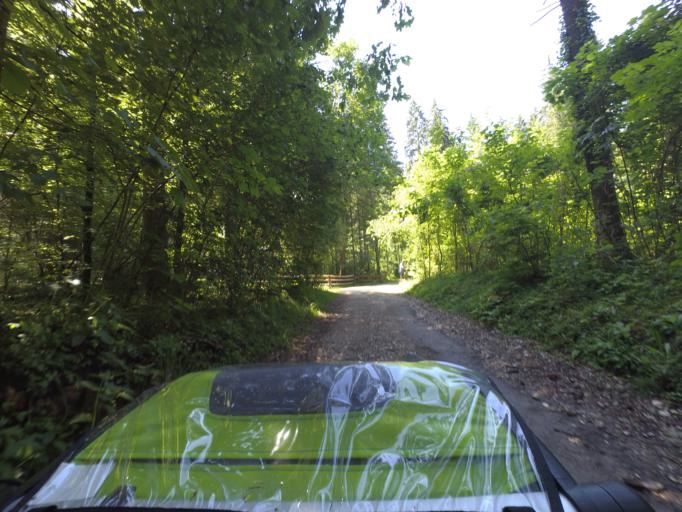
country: DE
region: Bavaria
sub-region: Upper Bavaria
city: Bayerisch Gmain
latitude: 47.7261
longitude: 12.9384
